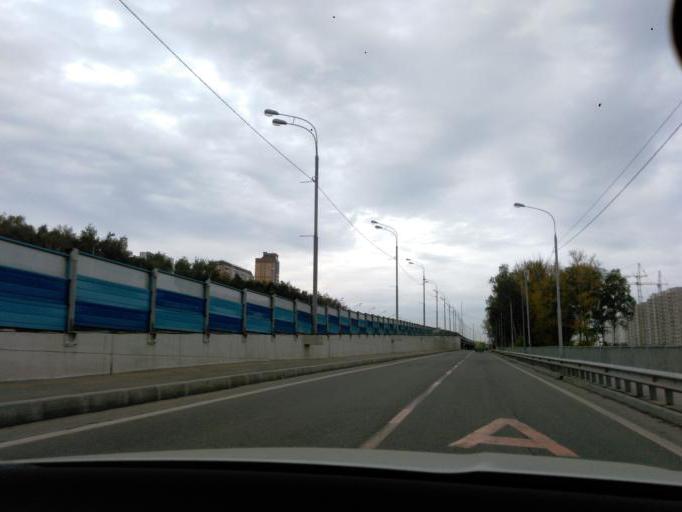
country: RU
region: Moscow
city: Severnyy
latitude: 55.9359
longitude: 37.5459
